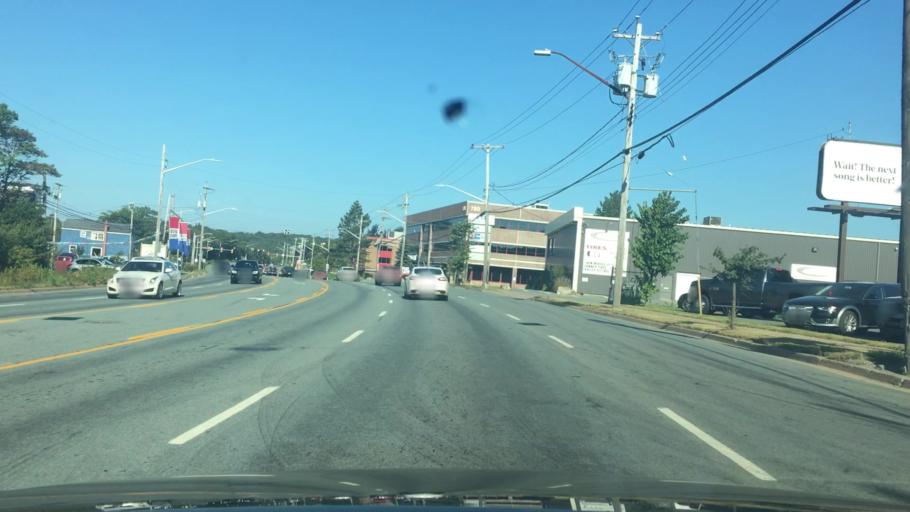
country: CA
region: Nova Scotia
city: Dartmouth
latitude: 44.7024
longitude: -63.6085
